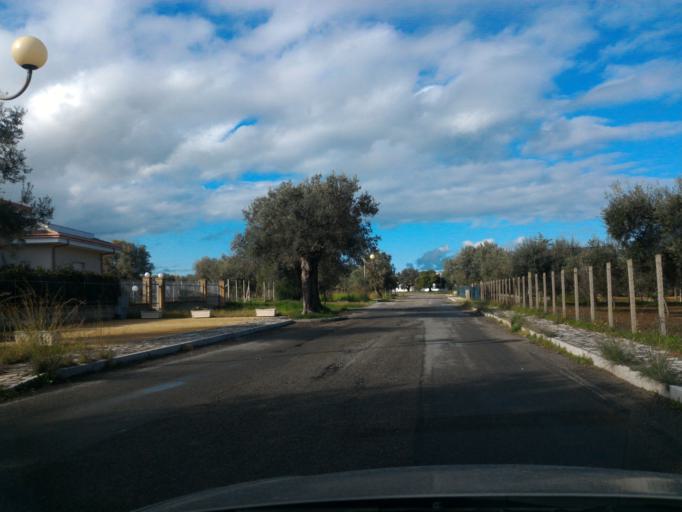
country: IT
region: Calabria
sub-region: Provincia di Crotone
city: Torretta
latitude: 39.4577
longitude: 17.0350
